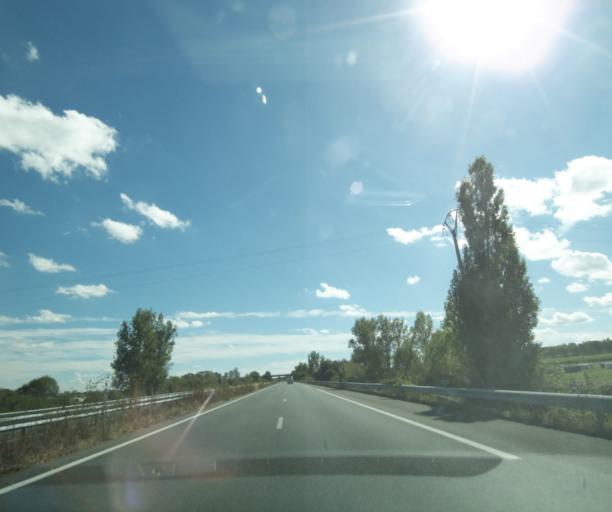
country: FR
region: Aquitaine
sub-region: Departement du Lot-et-Garonne
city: Damazan
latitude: 44.3368
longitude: 0.2536
